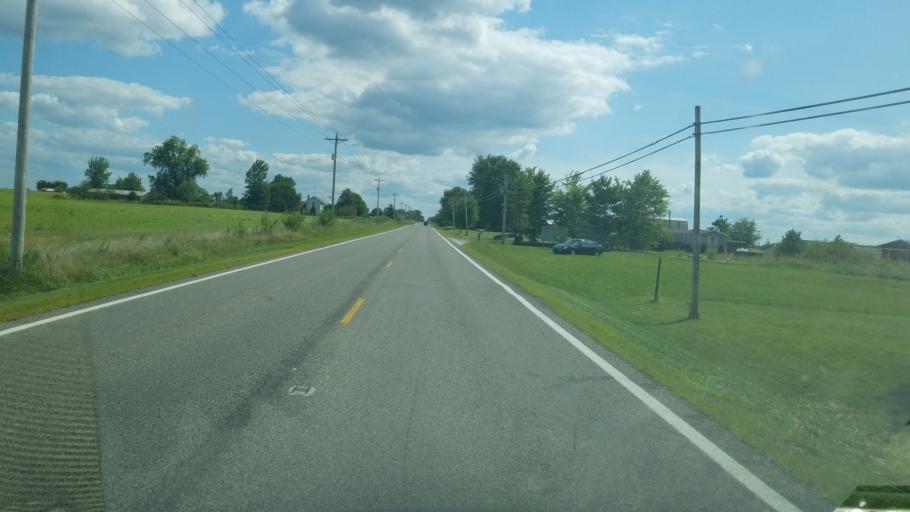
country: US
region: Ohio
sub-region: Logan County
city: Lakeview
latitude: 40.6219
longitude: -83.9755
